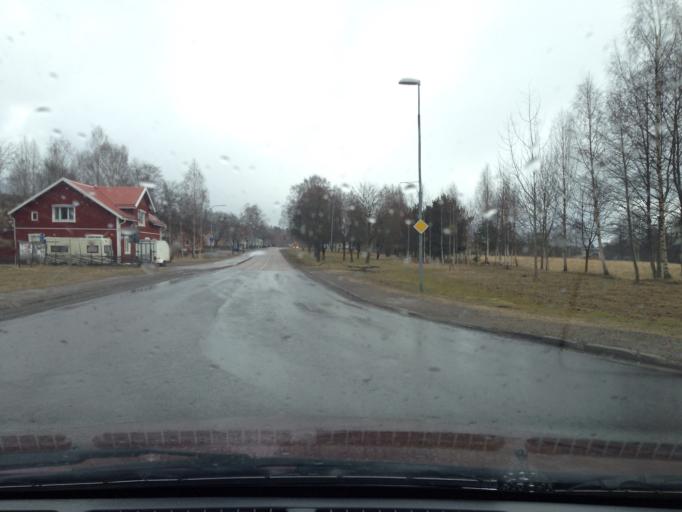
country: SE
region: Dalarna
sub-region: Smedjebackens Kommun
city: Smedjebacken
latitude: 60.1476
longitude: 15.3751
